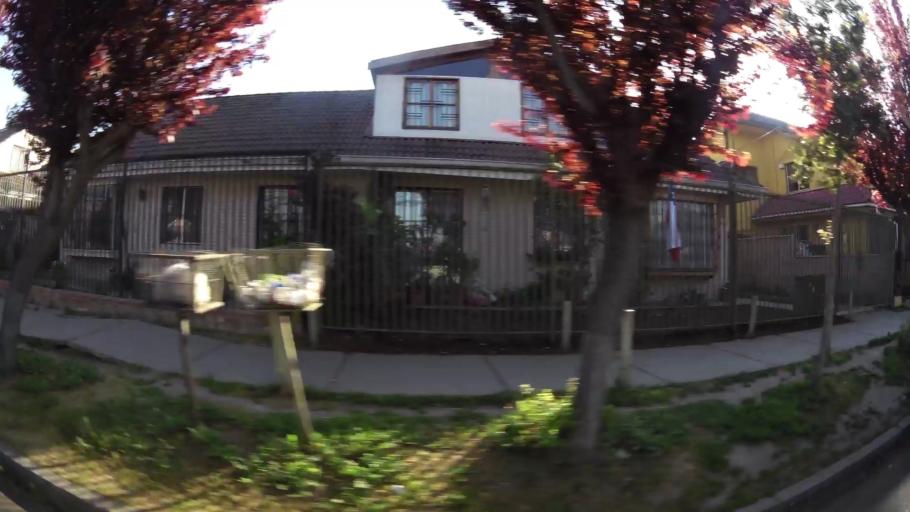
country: CL
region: Santiago Metropolitan
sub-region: Provincia de Santiago
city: Lo Prado
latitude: -33.4830
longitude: -70.7470
